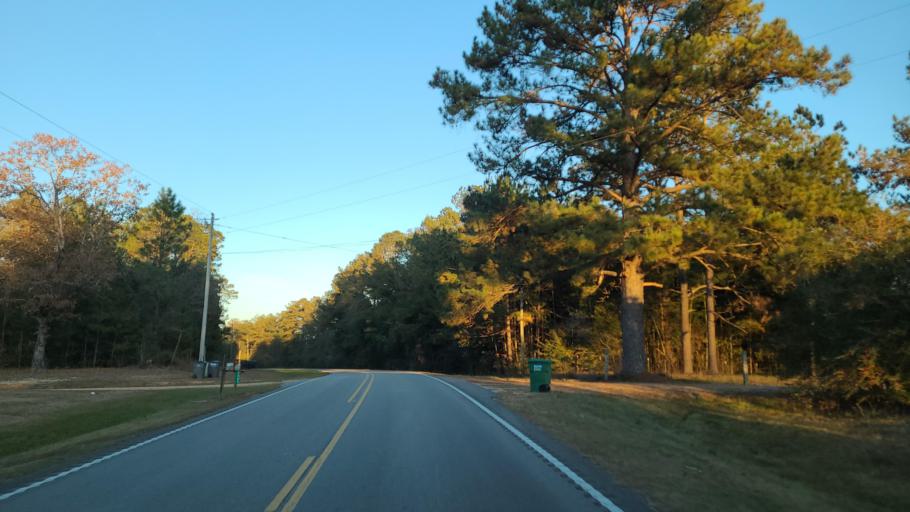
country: US
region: Mississippi
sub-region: Stone County
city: Wiggins
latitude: 31.0325
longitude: -89.2224
